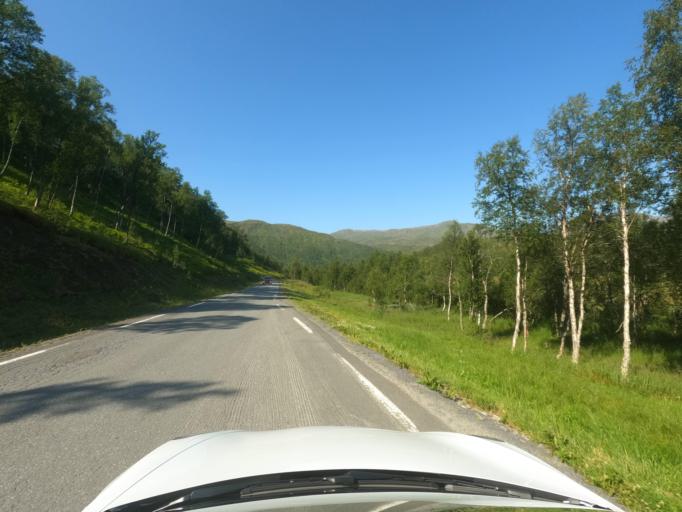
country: NO
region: Troms
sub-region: Skanland
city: Evenskjer
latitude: 68.3284
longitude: 16.5613
